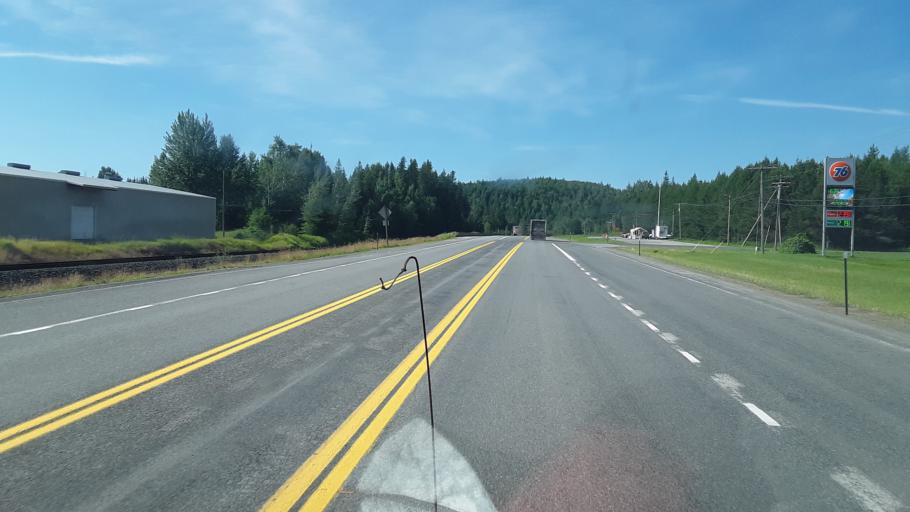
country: US
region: Idaho
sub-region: Bonner County
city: Ponderay
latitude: 48.4285
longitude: -116.4942
